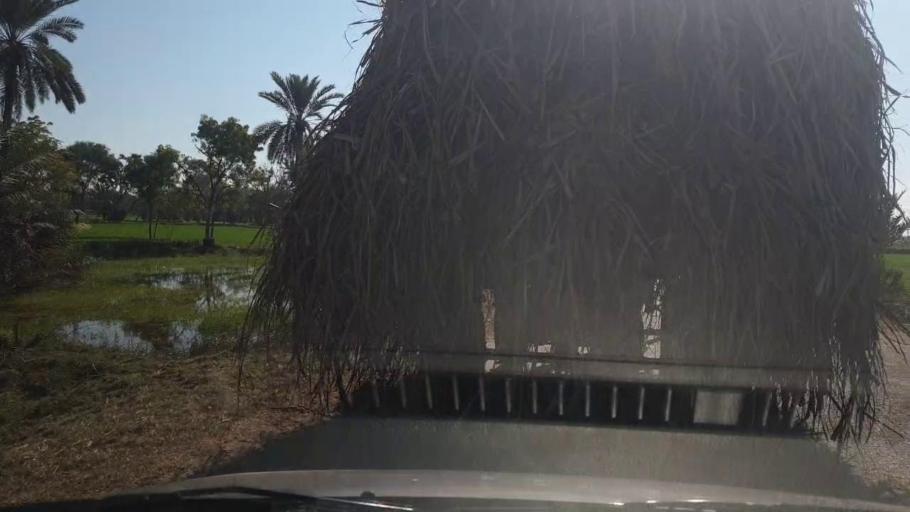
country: PK
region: Sindh
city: Bozdar
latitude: 27.1662
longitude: 68.6435
